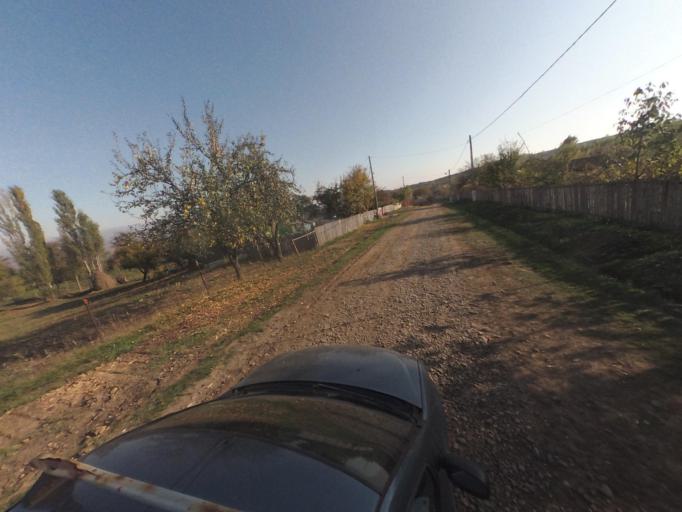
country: RO
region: Vaslui
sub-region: Comuna Bacesti
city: Bacesti
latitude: 46.8747
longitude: 27.1959
